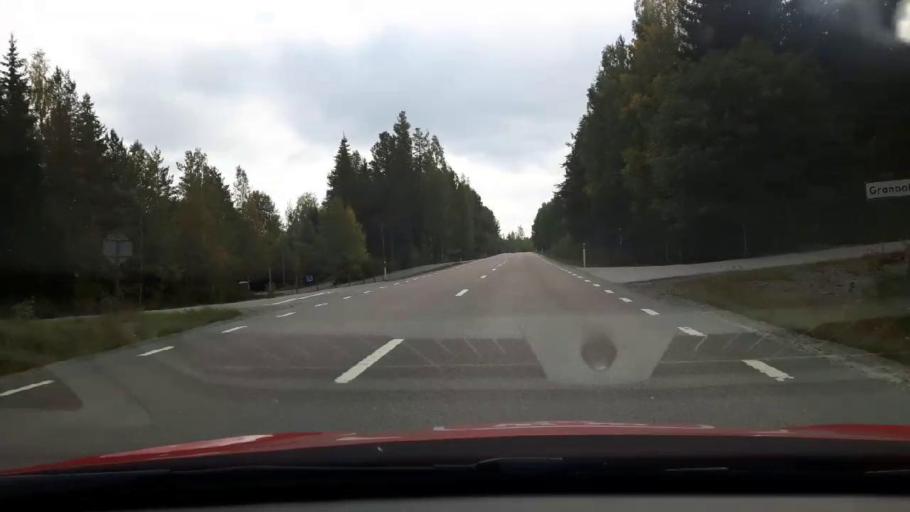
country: SE
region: Gaevleborg
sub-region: Bollnas Kommun
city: Kilafors
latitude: 61.2802
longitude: 16.5213
